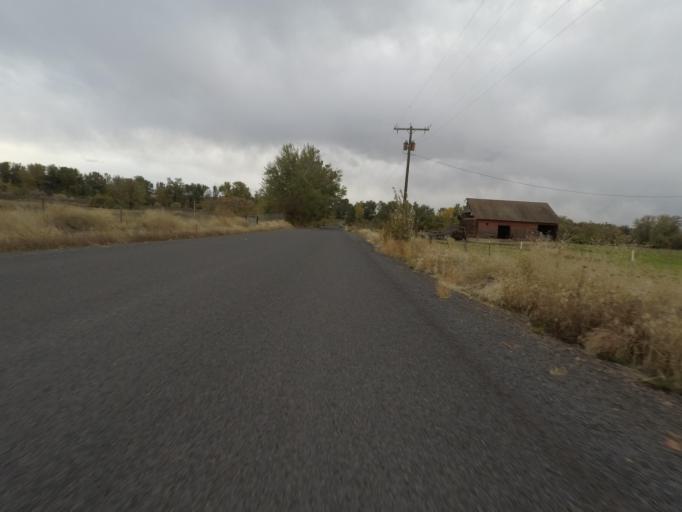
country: US
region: Washington
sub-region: Walla Walla County
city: Walla Walla East
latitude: 46.0848
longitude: -118.2525
